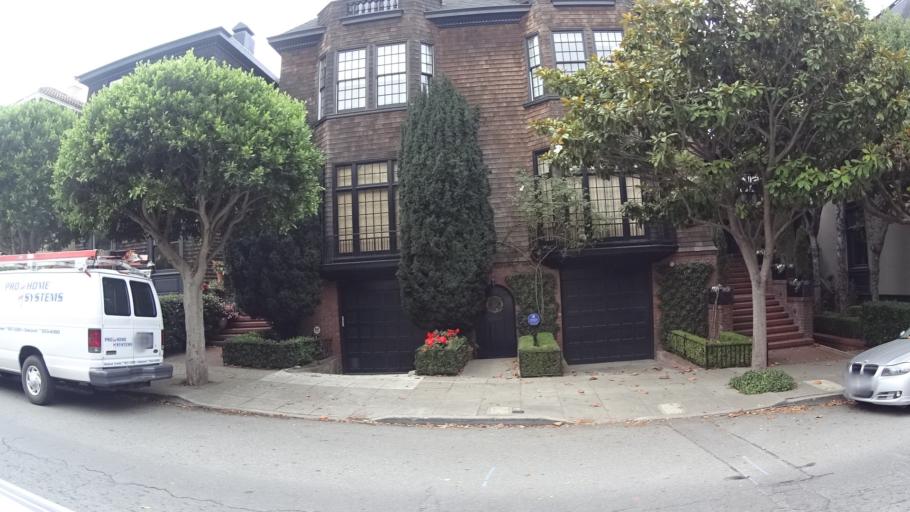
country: US
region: California
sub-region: San Francisco County
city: San Francisco
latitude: 37.7914
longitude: -122.4476
